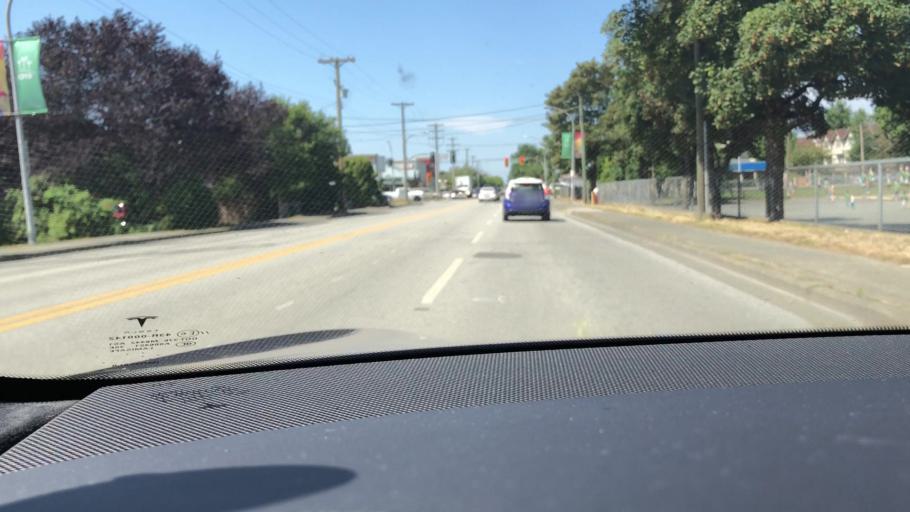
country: CA
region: British Columbia
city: Richmond
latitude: 49.1846
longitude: -123.0900
